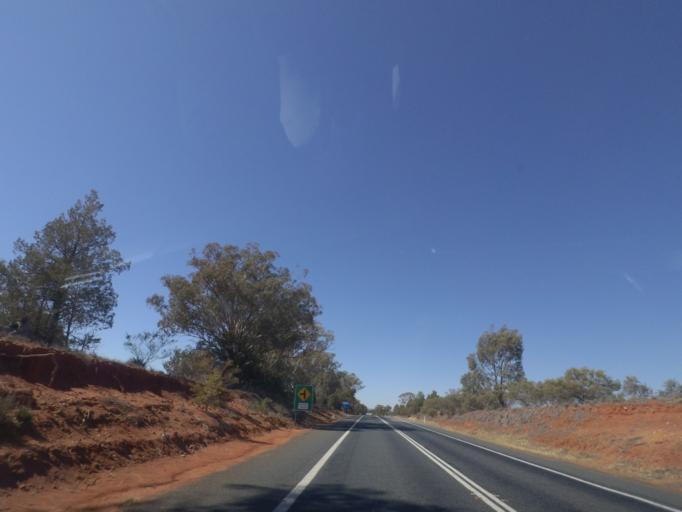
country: AU
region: New South Wales
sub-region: Bland
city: West Wyalong
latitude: -34.1799
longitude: 147.1135
